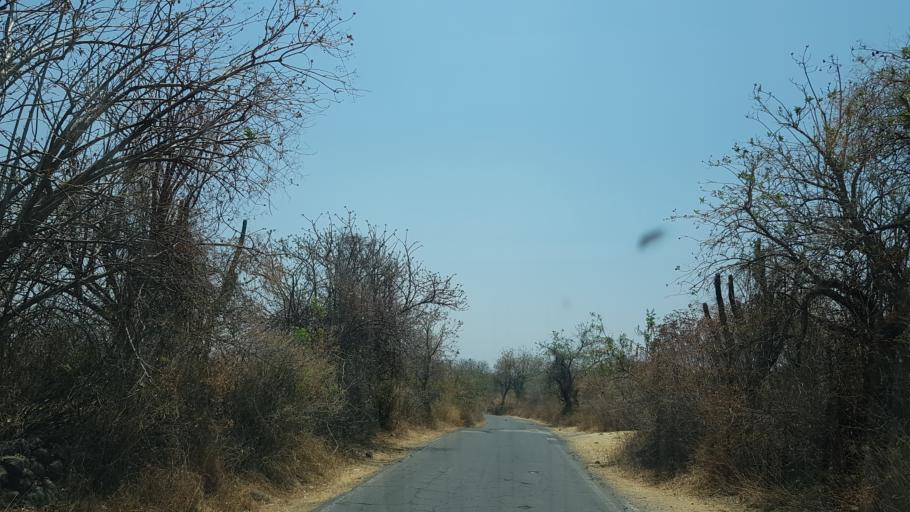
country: MX
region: Puebla
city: Huaquechula
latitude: 18.7844
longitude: -98.5453
